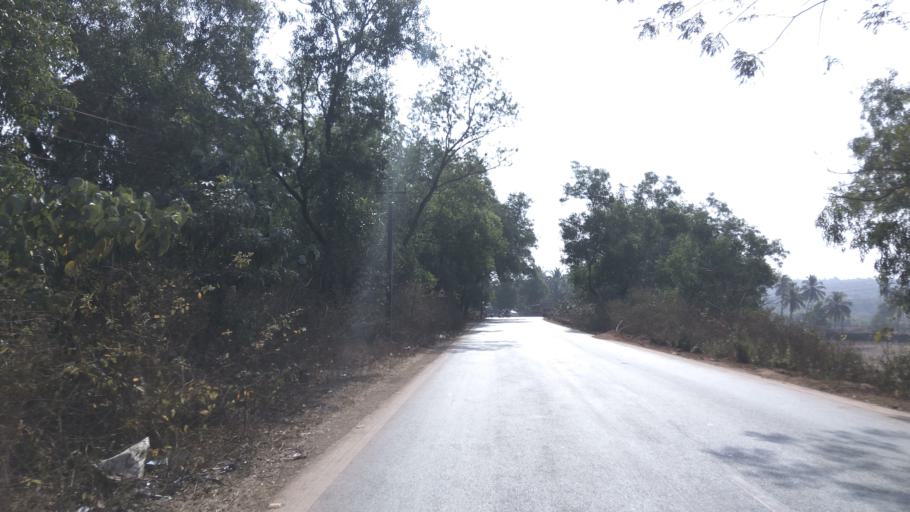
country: IN
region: Goa
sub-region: North Goa
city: Palle
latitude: 15.4139
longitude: 74.0798
